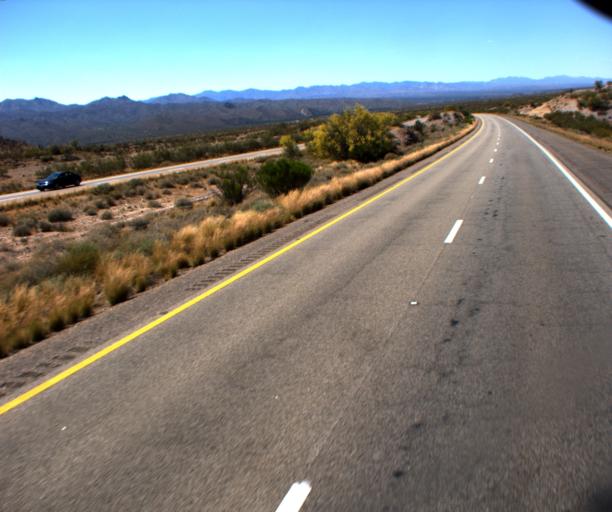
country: US
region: Arizona
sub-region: Yavapai County
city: Bagdad
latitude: 34.6202
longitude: -113.5305
